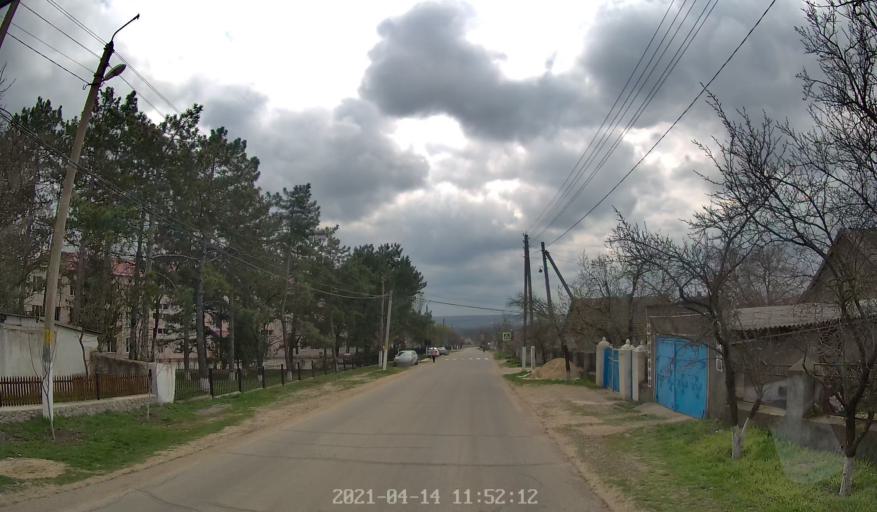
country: MD
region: Criuleni
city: Criuleni
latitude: 47.1703
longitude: 29.1953
